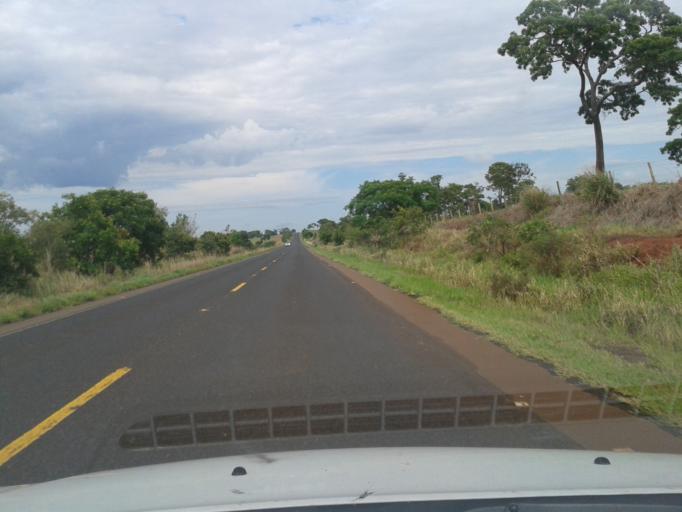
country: BR
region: Minas Gerais
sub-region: Iturama
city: Iturama
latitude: -19.5750
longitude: -49.9843
